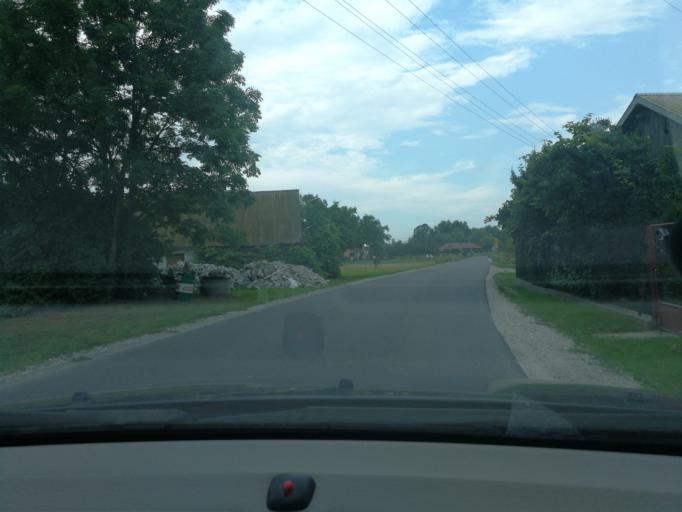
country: PL
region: Masovian Voivodeship
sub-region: Powiat warszawski zachodni
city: Bieniewice
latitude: 52.1059
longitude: 20.5550
